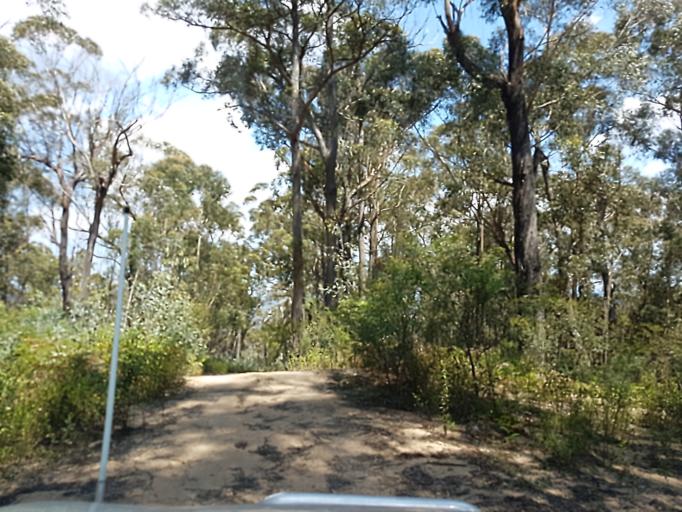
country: AU
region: Victoria
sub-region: East Gippsland
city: Lakes Entrance
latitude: -37.3999
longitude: 148.2983
